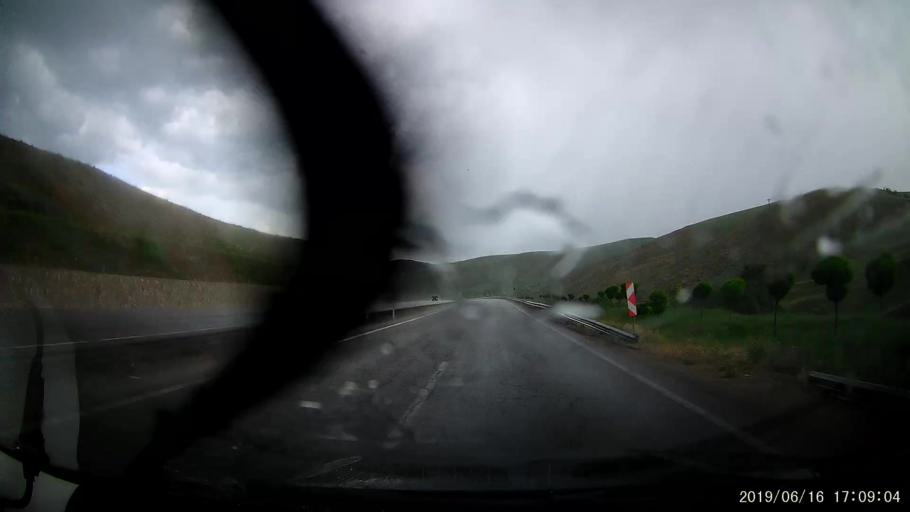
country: TR
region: Erzurum
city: Askale
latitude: 39.8998
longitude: 40.6542
